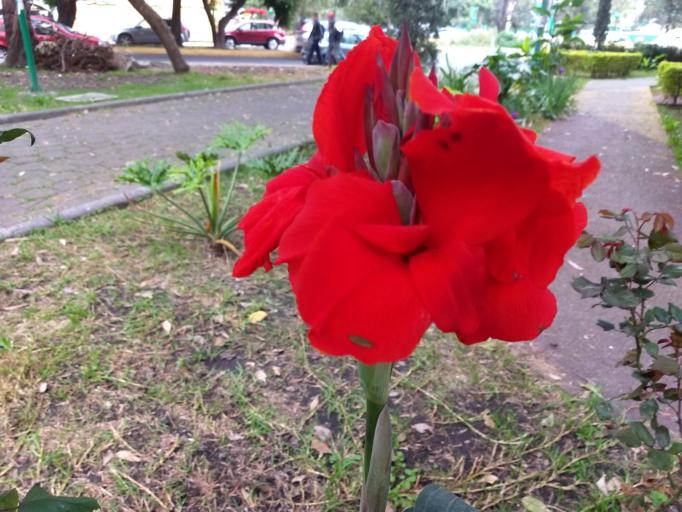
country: MX
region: Mexico City
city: Tlalpan
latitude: 19.3068
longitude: -99.1234
